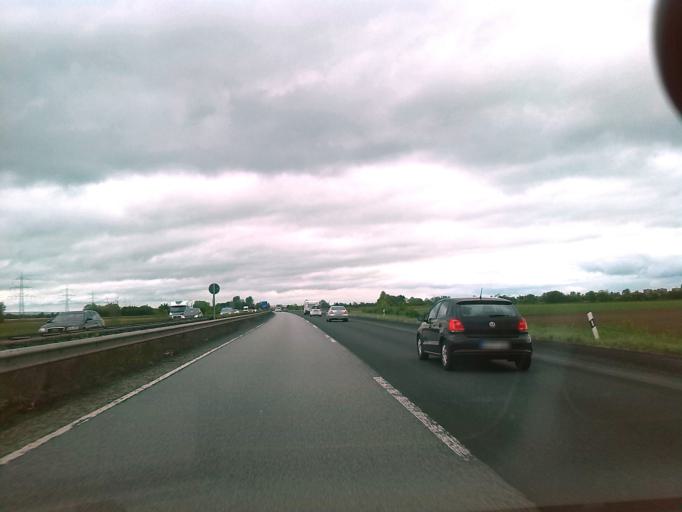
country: DE
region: Rheinland-Pfalz
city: Mutterstadt
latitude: 49.4193
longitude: 8.3391
